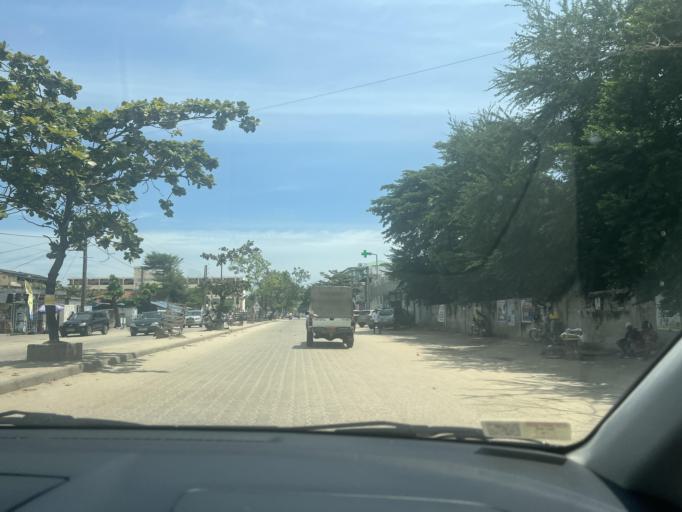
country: BJ
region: Littoral
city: Cotonou
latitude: 6.3748
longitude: 2.4468
